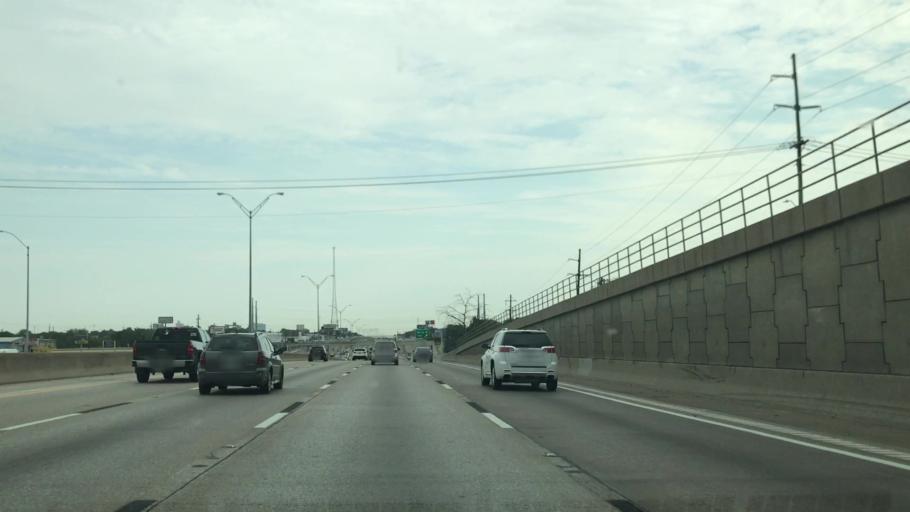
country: US
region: Texas
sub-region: Tarrant County
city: Fort Worth
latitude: 32.6980
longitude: -97.3205
